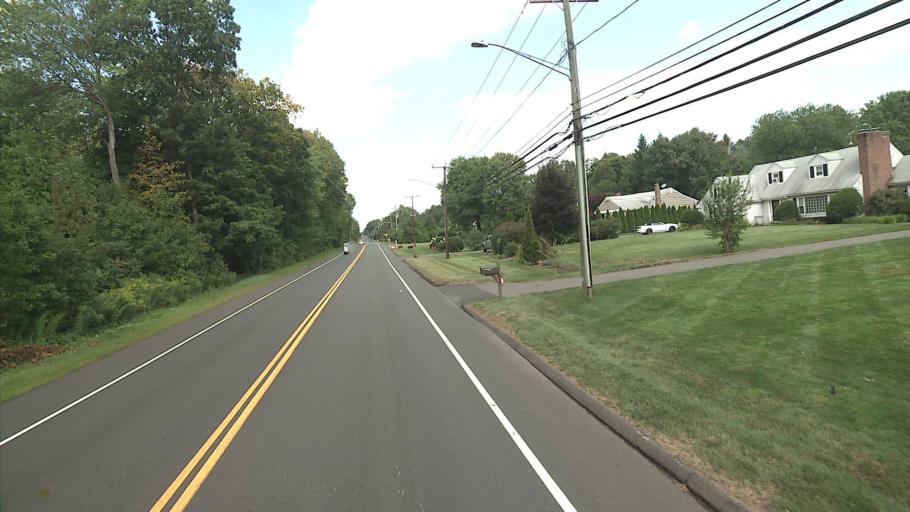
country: US
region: Connecticut
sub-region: Hartford County
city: Blue Hills
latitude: 41.8028
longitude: -72.7263
